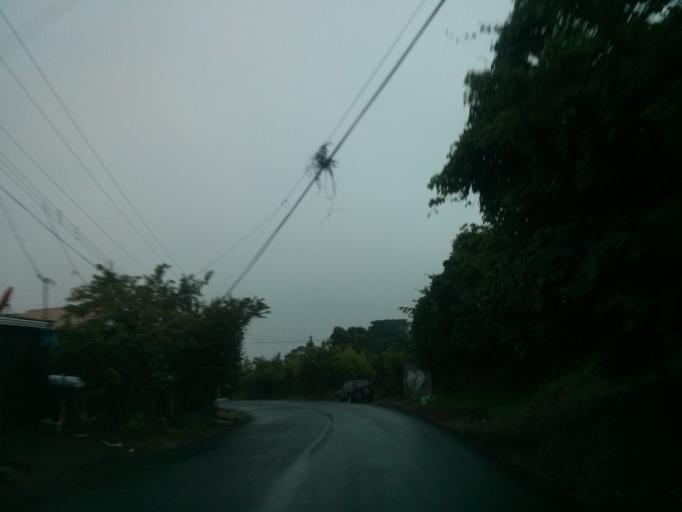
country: CR
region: Alajuela
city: Sabanilla
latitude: 10.1040
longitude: -84.1926
